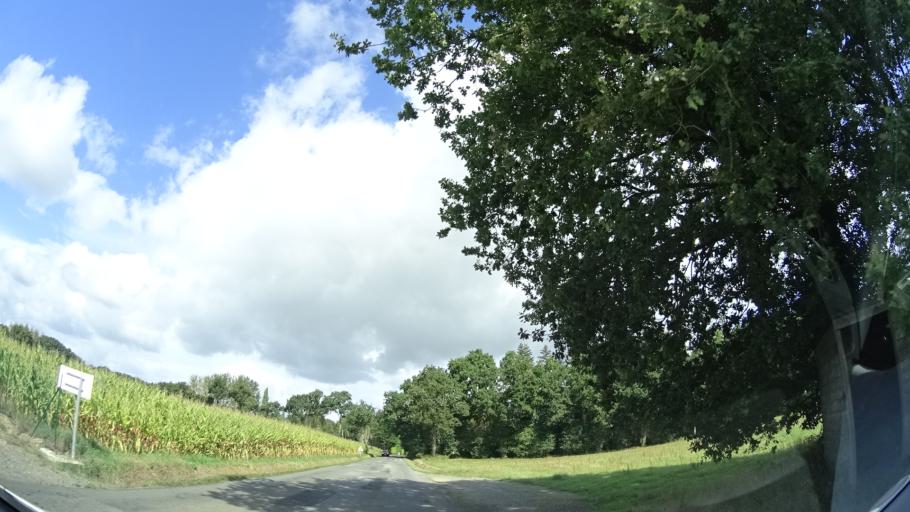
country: FR
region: Brittany
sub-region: Departement d'Ille-et-Vilaine
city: Montreuil-sur-Ille
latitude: 48.3342
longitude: -1.6895
